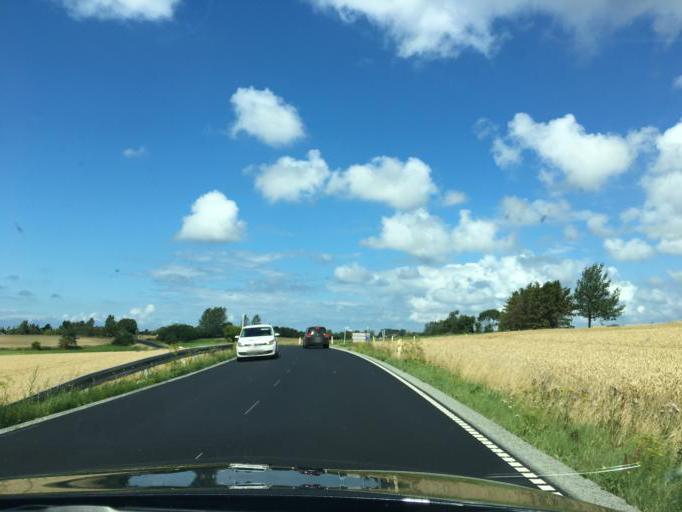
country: DK
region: Capital Region
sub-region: Gribskov Kommune
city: Helsinge
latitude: 56.0644
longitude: 12.2027
